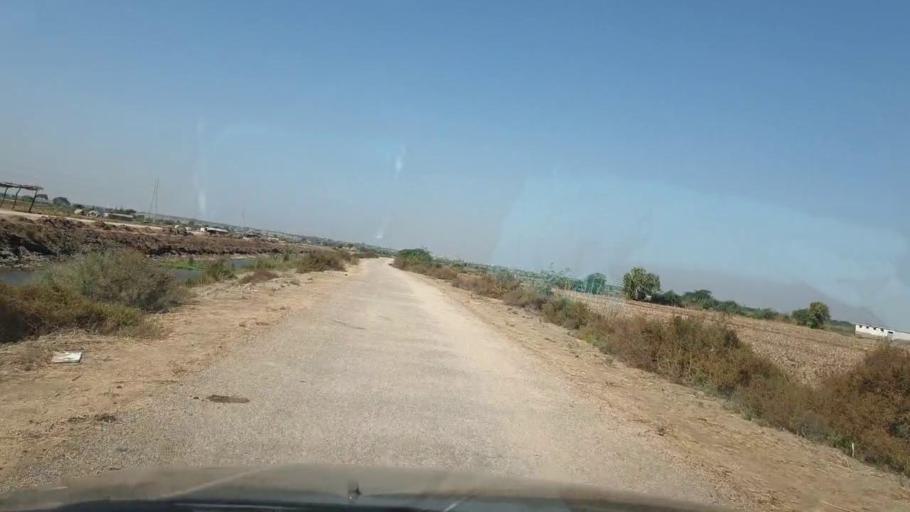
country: PK
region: Sindh
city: Thatta
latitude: 24.7234
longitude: 67.9282
